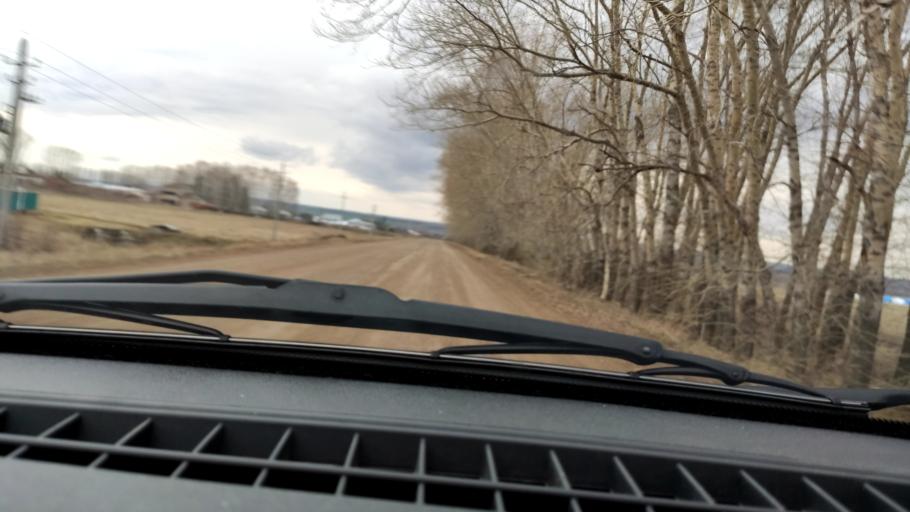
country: RU
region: Bashkortostan
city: Semiletka
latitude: 55.2885
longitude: 54.6732
